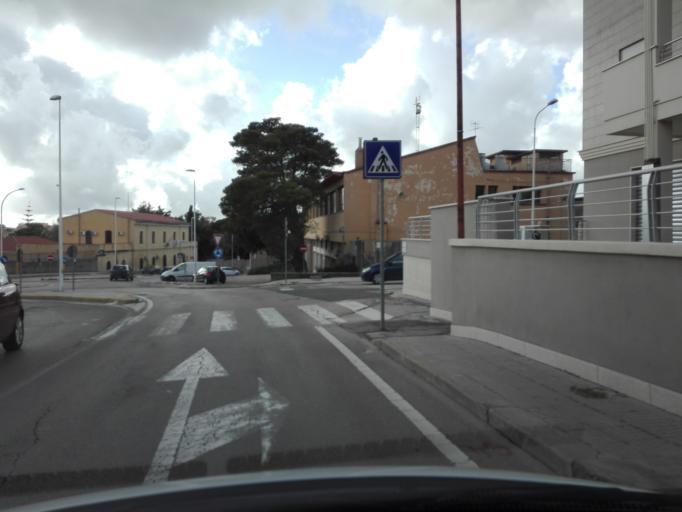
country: IT
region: Sardinia
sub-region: Provincia di Sassari
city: Sassari
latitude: 40.7165
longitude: 8.5765
